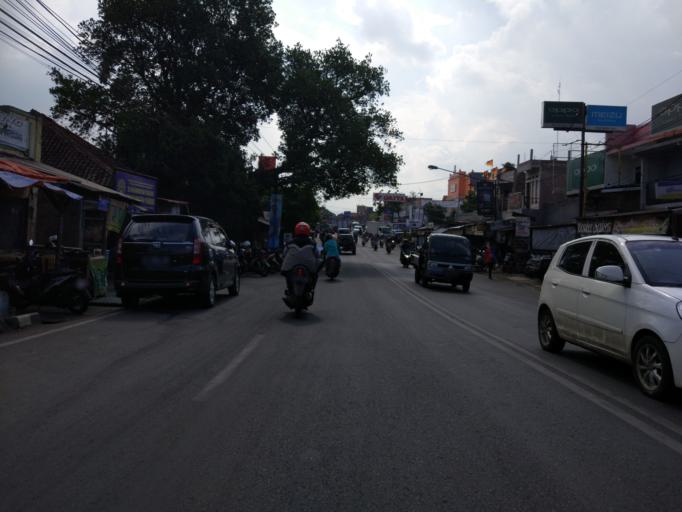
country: ID
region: West Java
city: Cileunyi
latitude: -6.9158
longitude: 107.7045
